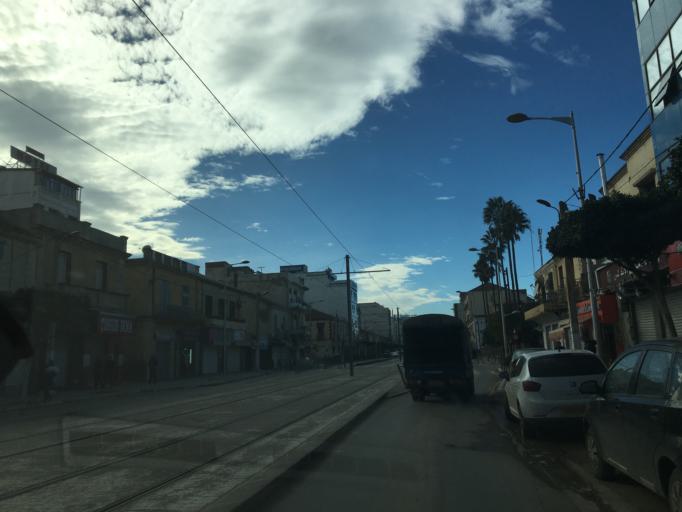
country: DZ
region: Alger
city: Bordj el Kiffan
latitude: 36.7474
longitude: 3.1919
